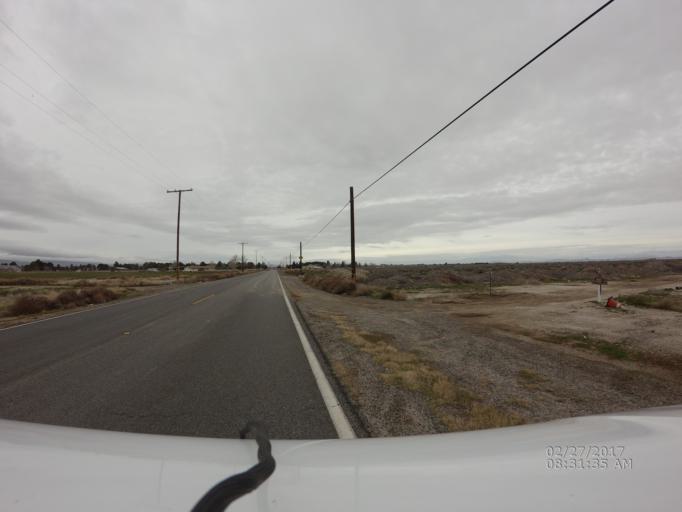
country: US
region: California
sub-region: Los Angeles County
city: Lancaster
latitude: 34.7046
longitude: -118.0477
